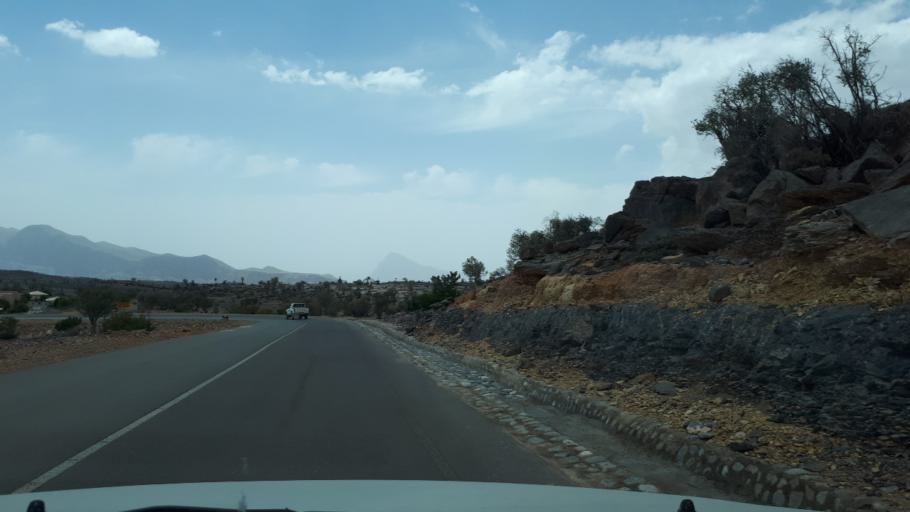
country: OM
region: Muhafazat ad Dakhiliyah
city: Bahla'
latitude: 23.2091
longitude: 57.2003
